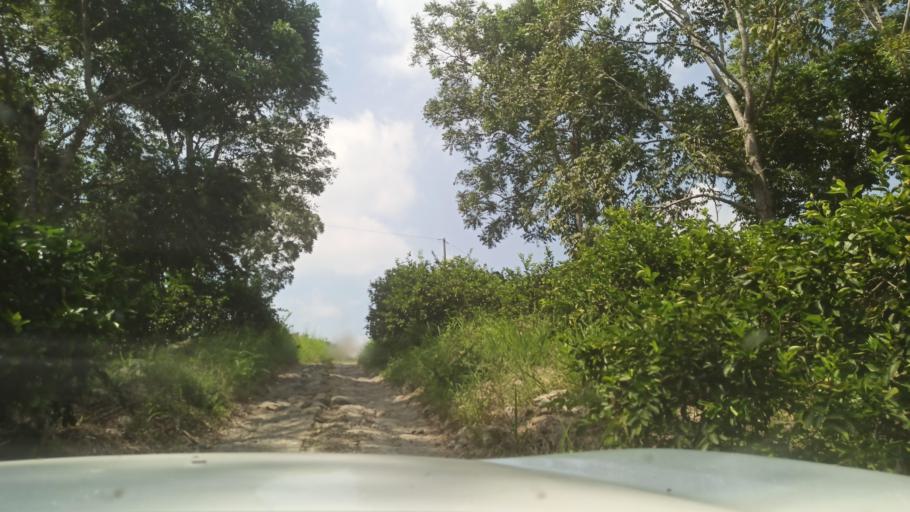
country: MX
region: Veracruz
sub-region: Atzalan
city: Colonias Pedernales
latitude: 20.0538
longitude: -96.9965
